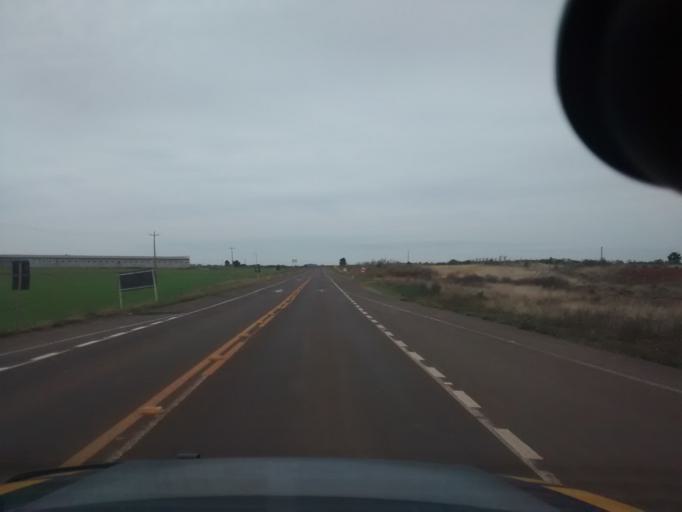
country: BR
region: Rio Grande do Sul
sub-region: Vacaria
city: Vacaria
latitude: -28.4286
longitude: -51.0230
